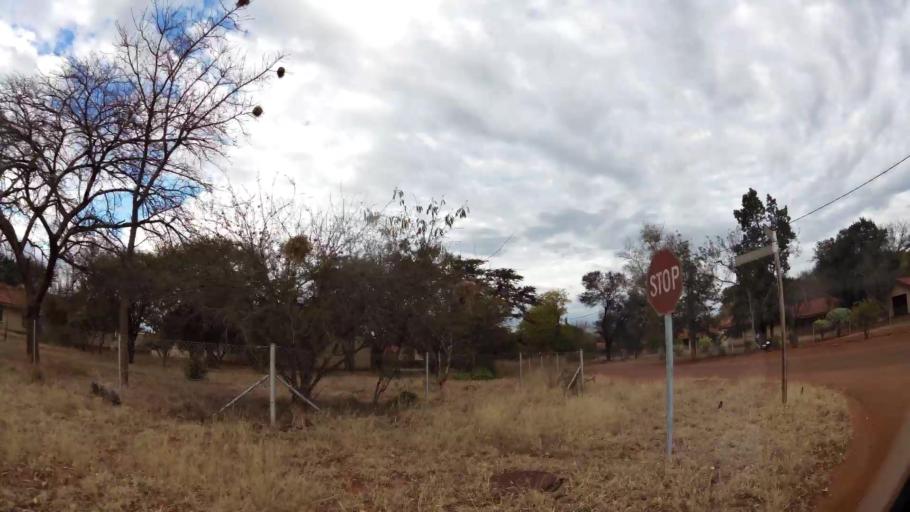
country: ZA
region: Limpopo
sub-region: Waterberg District Municipality
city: Modimolle
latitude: -24.5047
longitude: 28.7190
